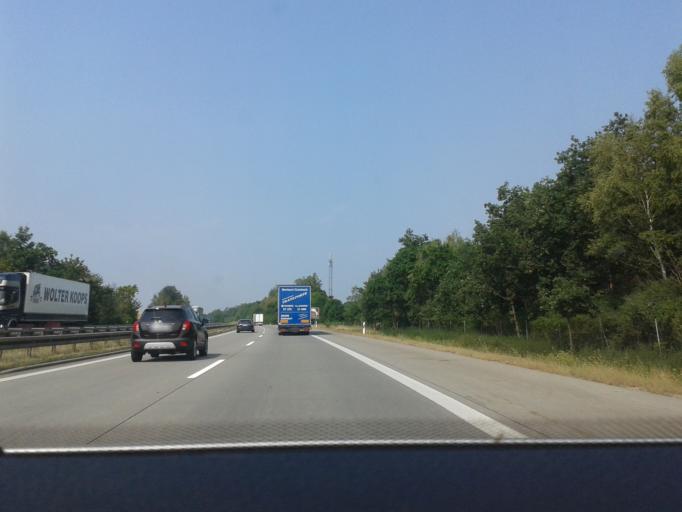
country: DE
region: Saxony
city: Nerchau
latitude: 51.2592
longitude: 12.7752
